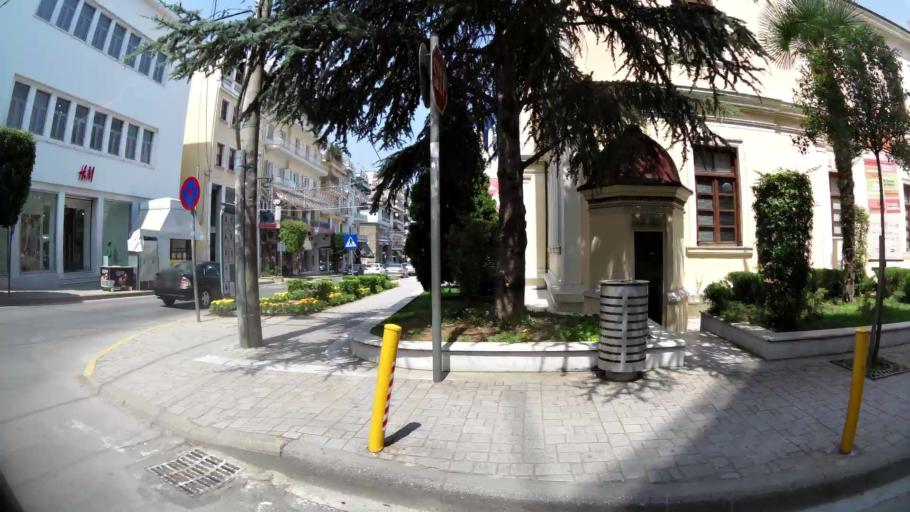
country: GR
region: Central Macedonia
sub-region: Nomos Imathias
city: Veroia
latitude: 40.5228
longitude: 22.2041
